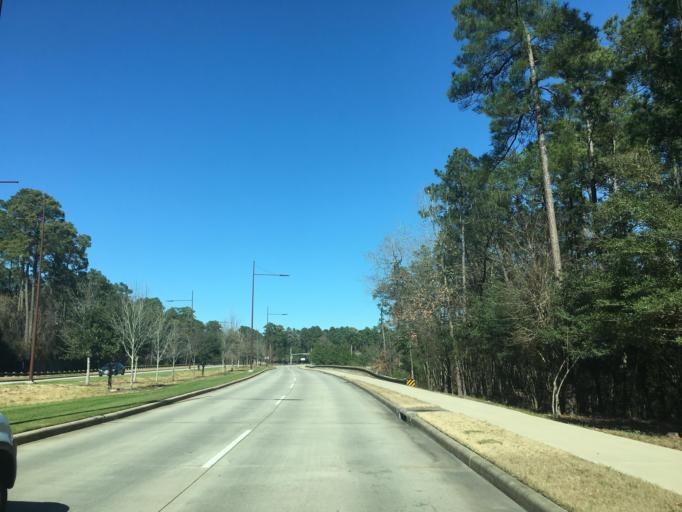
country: US
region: Texas
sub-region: Harris County
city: Spring
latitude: 30.1019
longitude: -95.4412
